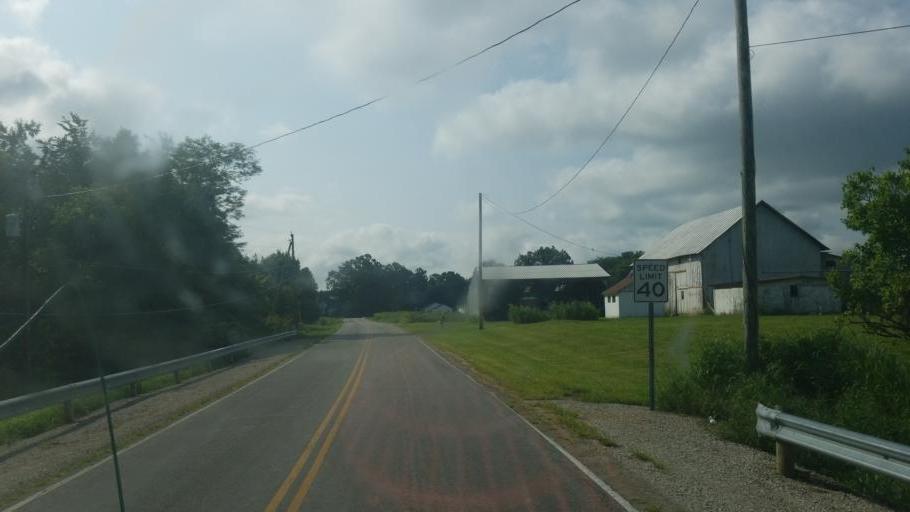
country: US
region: Ohio
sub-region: Morrow County
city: Cardington
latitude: 40.5756
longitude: -82.9986
